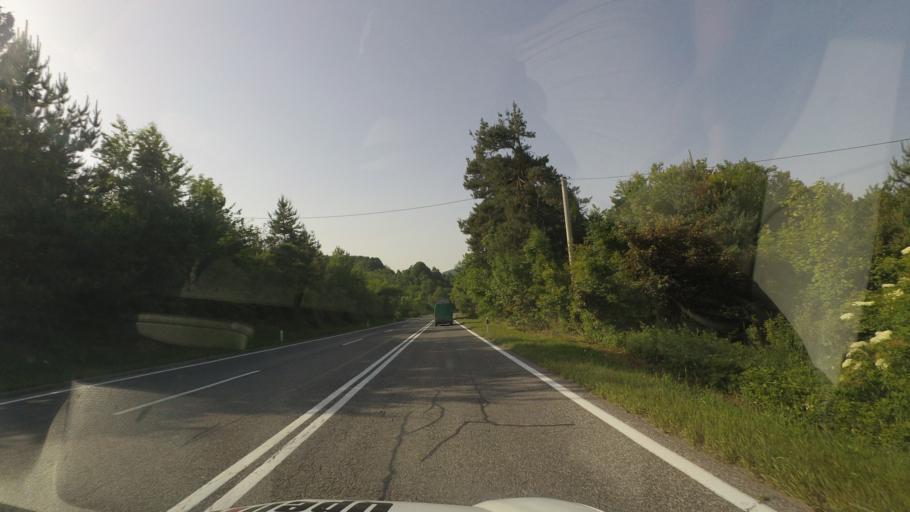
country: HR
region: Karlovacka
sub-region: Grad Karlovac
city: Slunj
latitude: 45.0765
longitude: 15.5762
